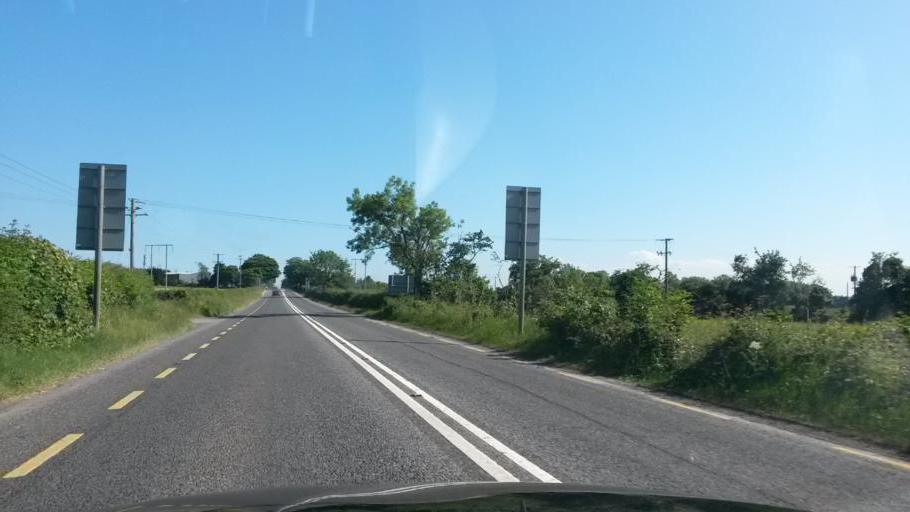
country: IE
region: Leinster
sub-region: An Mhi
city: Ratoath
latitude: 53.5563
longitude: -6.4387
